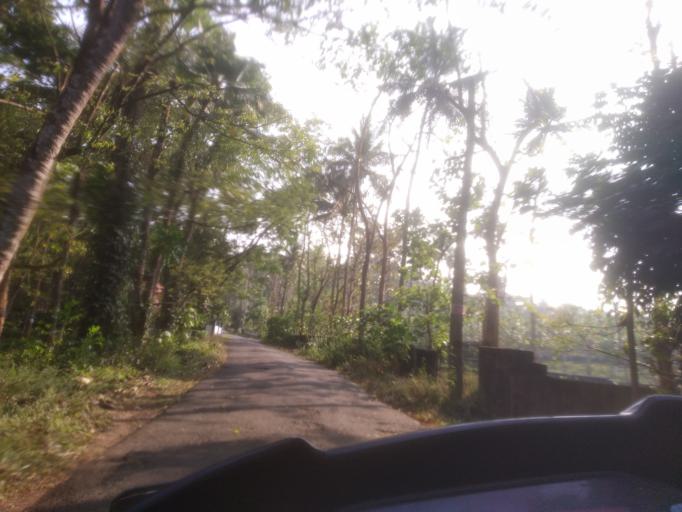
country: IN
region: Kerala
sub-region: Ernakulam
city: Piravam
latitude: 9.8479
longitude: 76.5285
